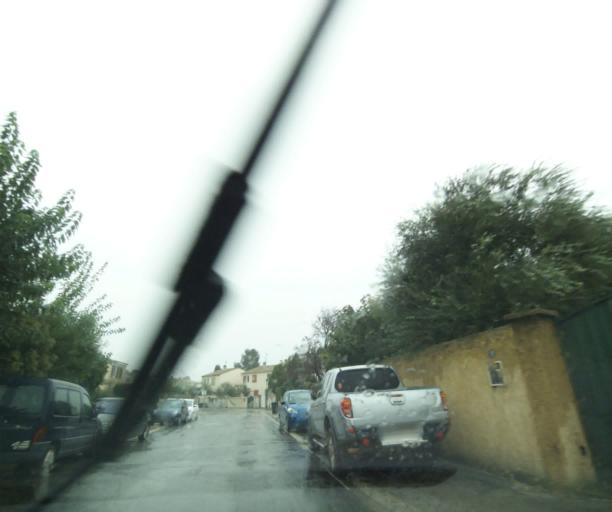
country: FR
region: Languedoc-Roussillon
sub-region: Departement du Gard
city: Milhaud
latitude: 43.7917
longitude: 4.3105
